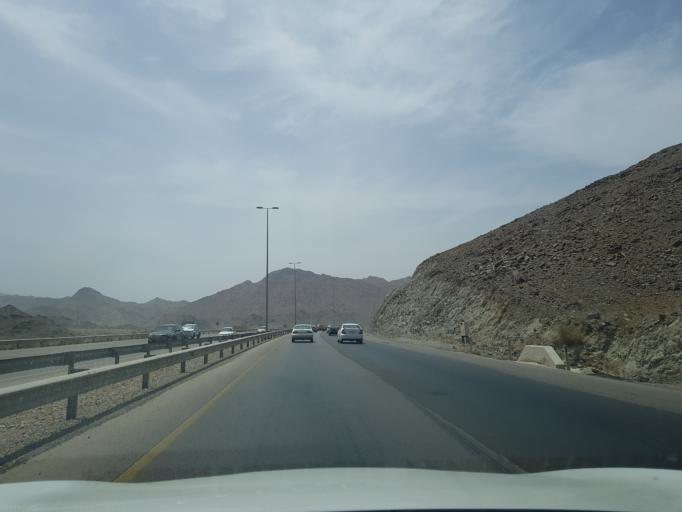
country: OM
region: Muhafazat ad Dakhiliyah
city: Bidbid
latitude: 23.4732
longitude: 58.1960
